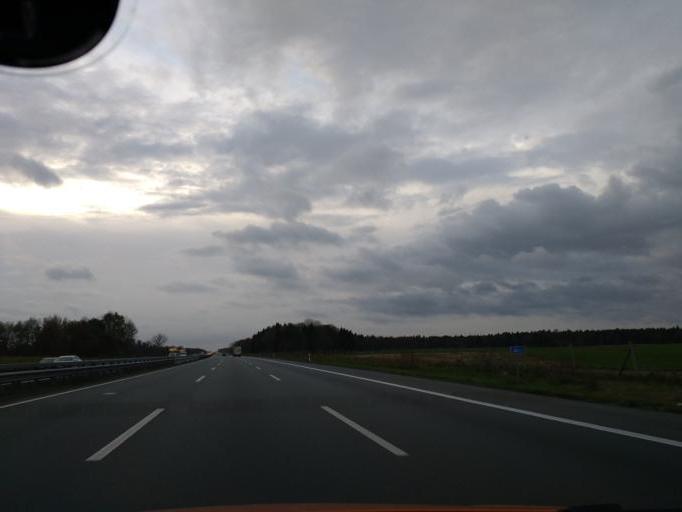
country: DE
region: Lower Saxony
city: Halvesbostel
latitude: 53.3255
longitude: 9.5930
